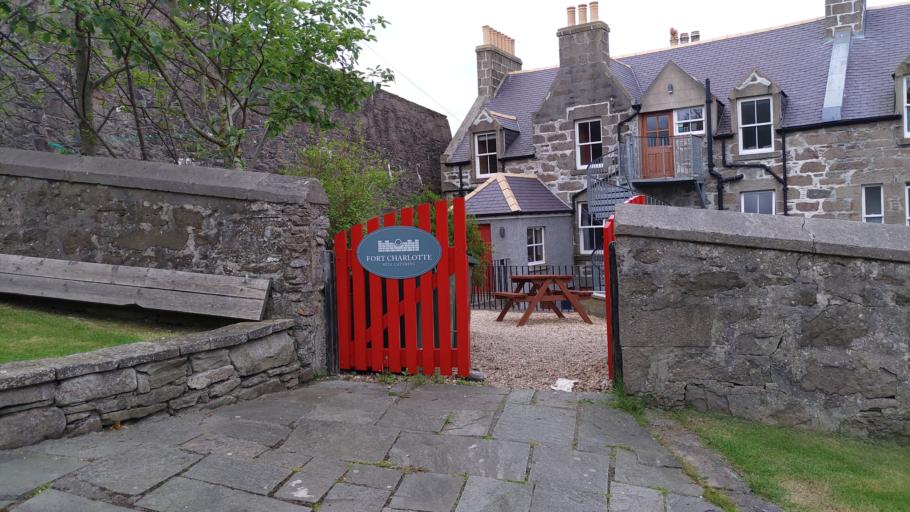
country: GB
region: Scotland
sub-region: Shetland Islands
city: Shetland
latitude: 60.1549
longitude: -1.1444
